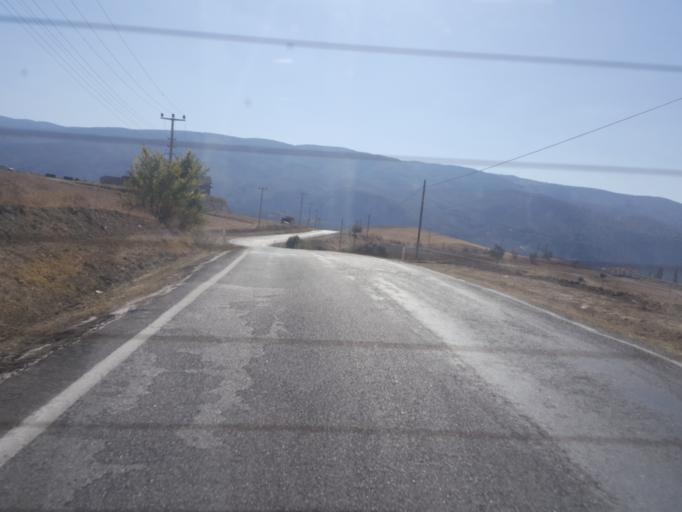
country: TR
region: Kastamonu
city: Tosya
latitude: 40.9924
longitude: 34.0714
